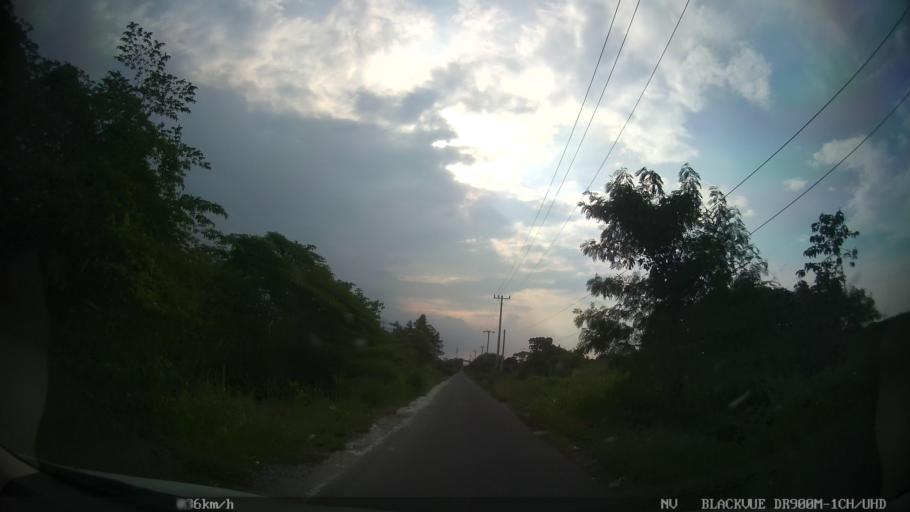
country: ID
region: North Sumatra
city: Medan
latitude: 3.6054
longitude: 98.7328
